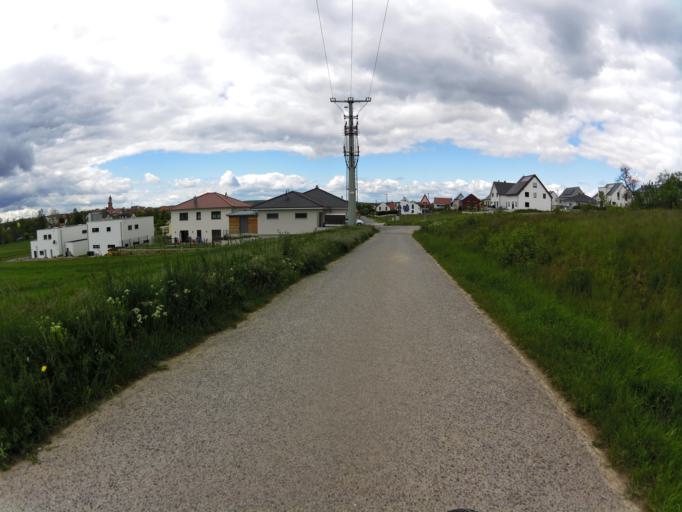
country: DE
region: Bavaria
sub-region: Regierungsbezirk Unterfranken
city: Volkach
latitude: 49.8702
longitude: 10.2341
